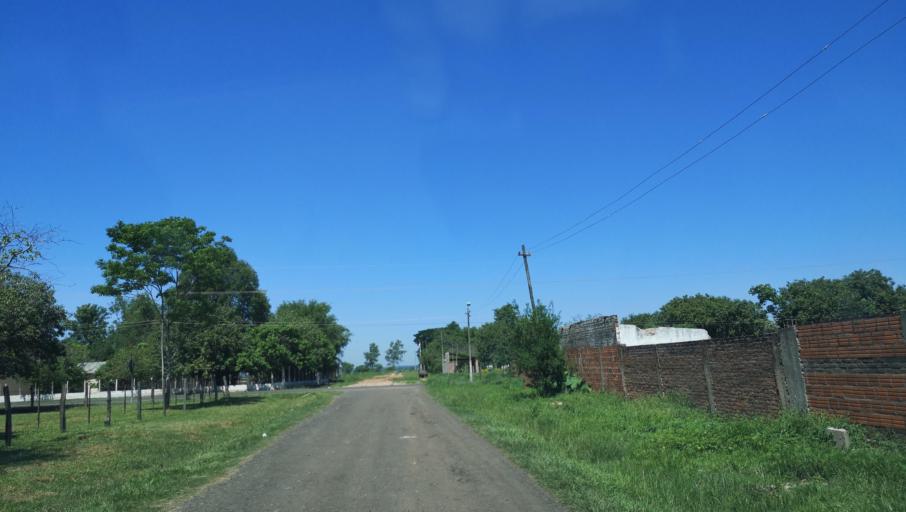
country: PY
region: Caaguazu
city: Carayao
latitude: -25.1945
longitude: -56.4056
